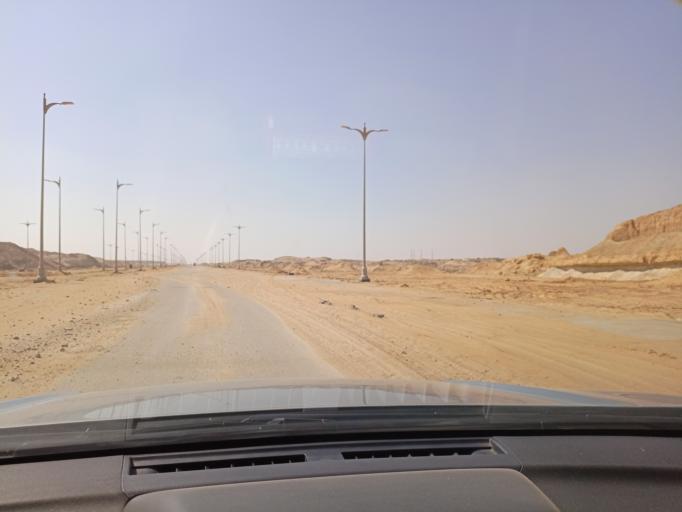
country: EG
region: Muhafazat al Qalyubiyah
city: Al Khankah
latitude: 30.0084
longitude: 31.6236
